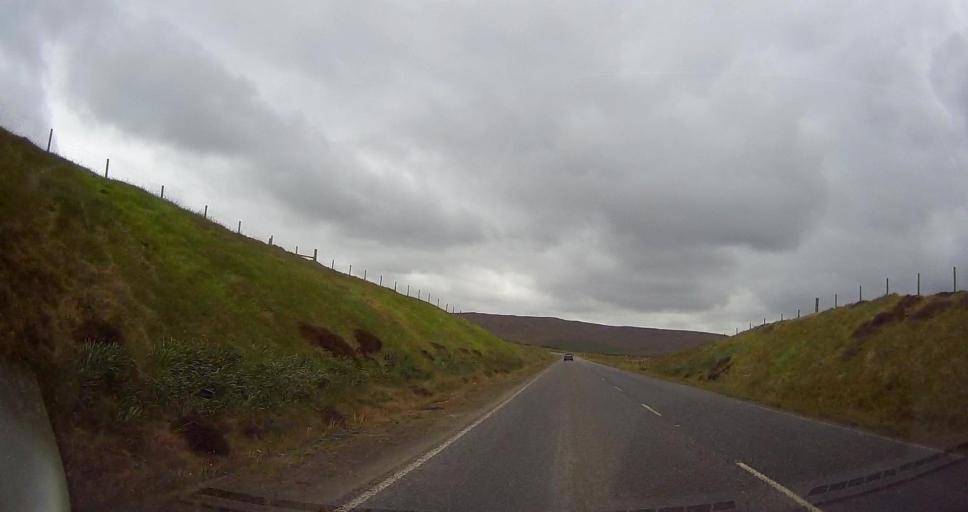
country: GB
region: Scotland
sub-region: Shetland Islands
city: Lerwick
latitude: 60.3769
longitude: -1.3392
